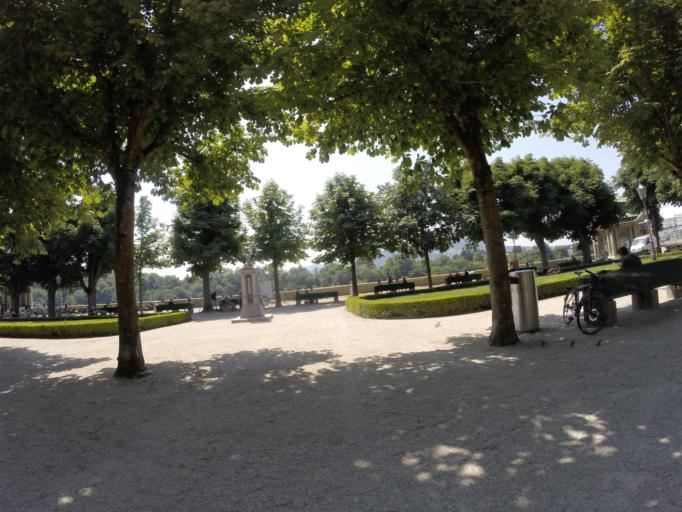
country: CH
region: Bern
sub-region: Bern-Mittelland District
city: Bern
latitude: 46.9467
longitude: 7.4519
